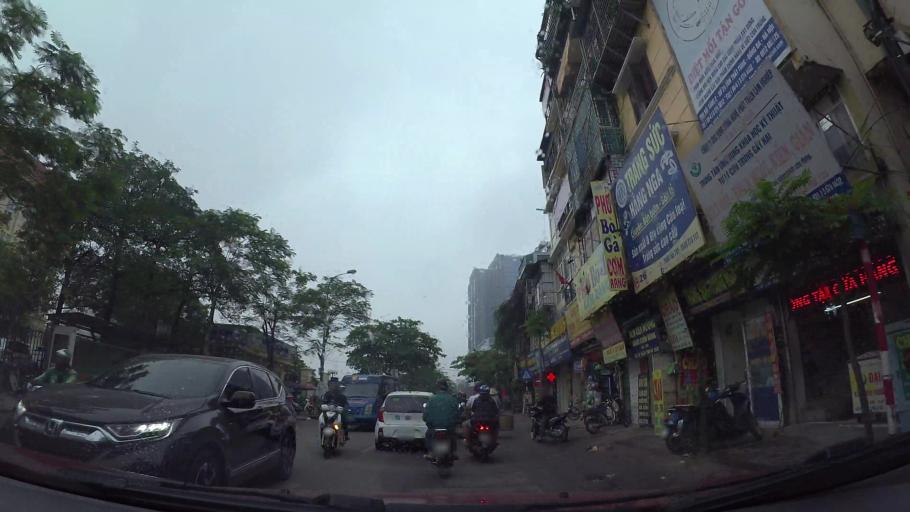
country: VN
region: Ha Noi
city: Dong Da
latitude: 21.0023
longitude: 105.8297
